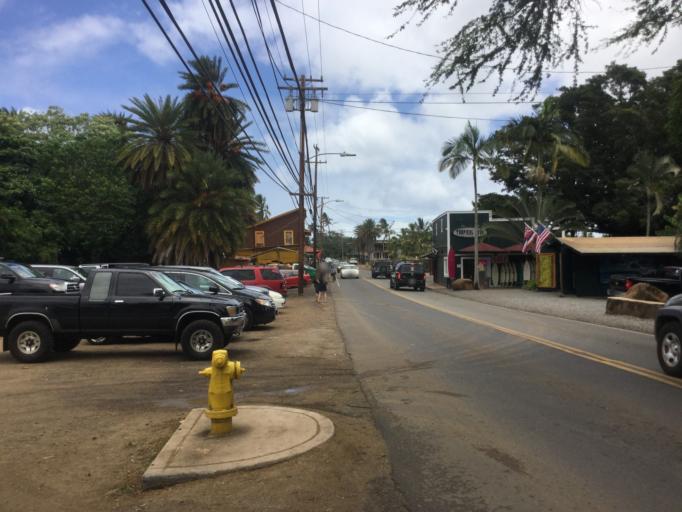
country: US
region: Hawaii
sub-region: Honolulu County
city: Hale'iwa
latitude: 21.5939
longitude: -158.1034
